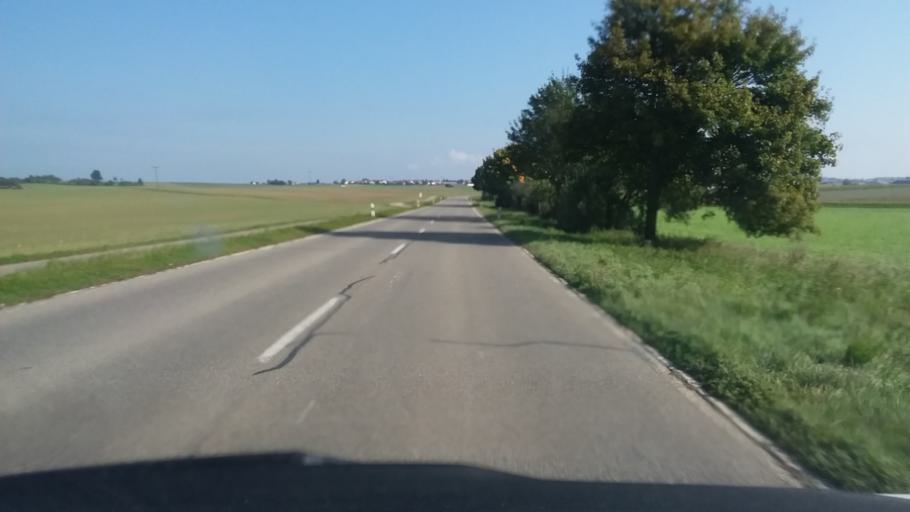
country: DE
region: Baden-Wuerttemberg
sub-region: Tuebingen Region
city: Nellingen
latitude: 48.5277
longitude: 9.7744
